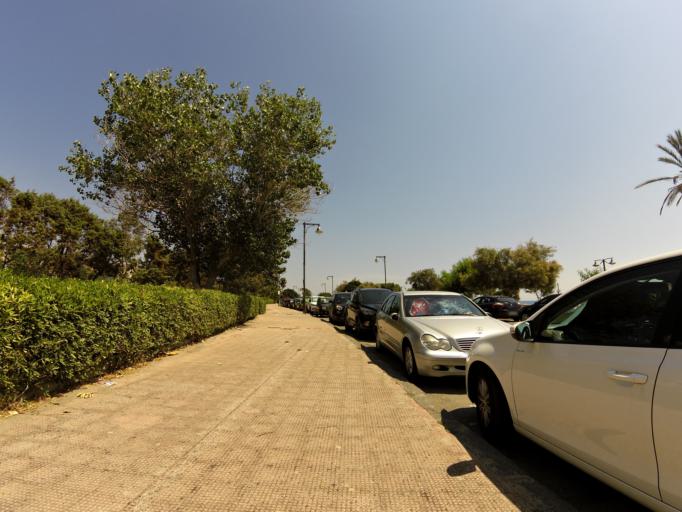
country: IT
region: Calabria
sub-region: Provincia di Reggio Calabria
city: Roccella Ionica
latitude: 38.3232
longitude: 16.4125
